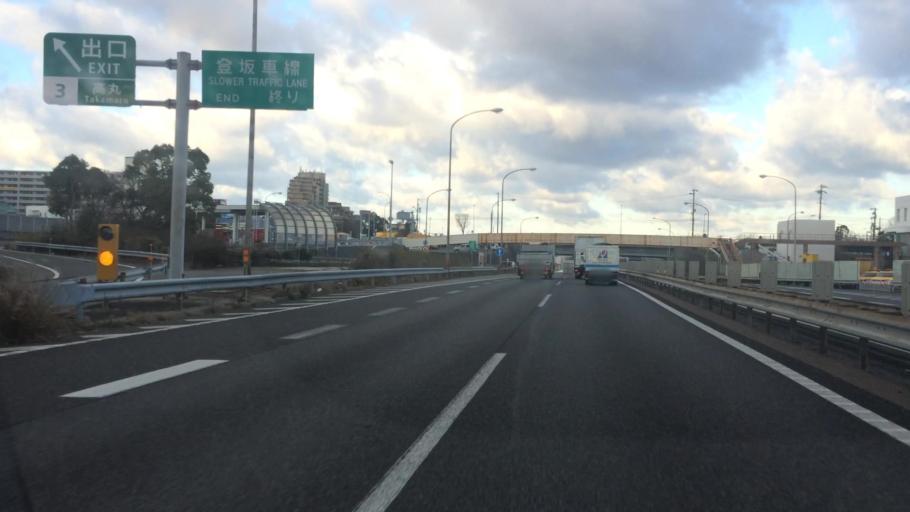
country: JP
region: Hyogo
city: Akashi
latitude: 34.6475
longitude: 135.0540
